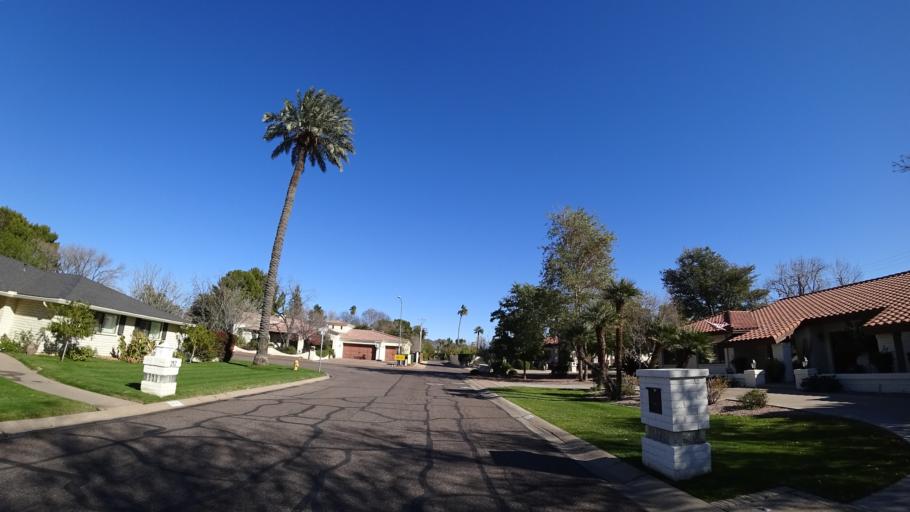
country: US
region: Arizona
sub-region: Maricopa County
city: Phoenix
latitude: 33.5419
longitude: -112.0699
